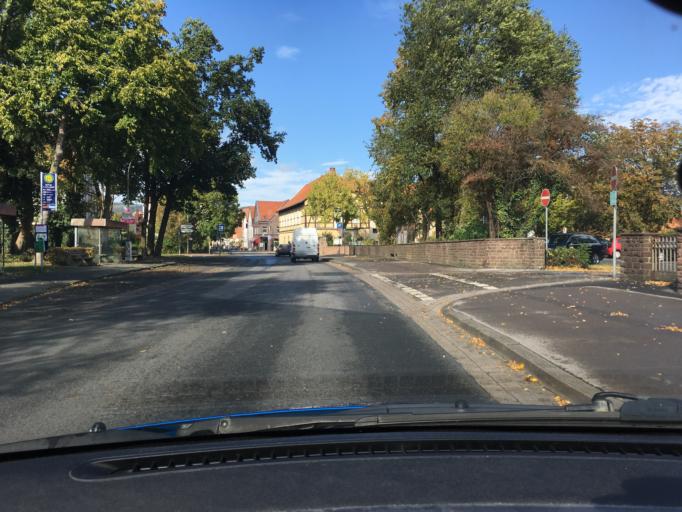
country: DE
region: Lower Saxony
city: Springe
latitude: 52.2063
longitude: 9.5559
